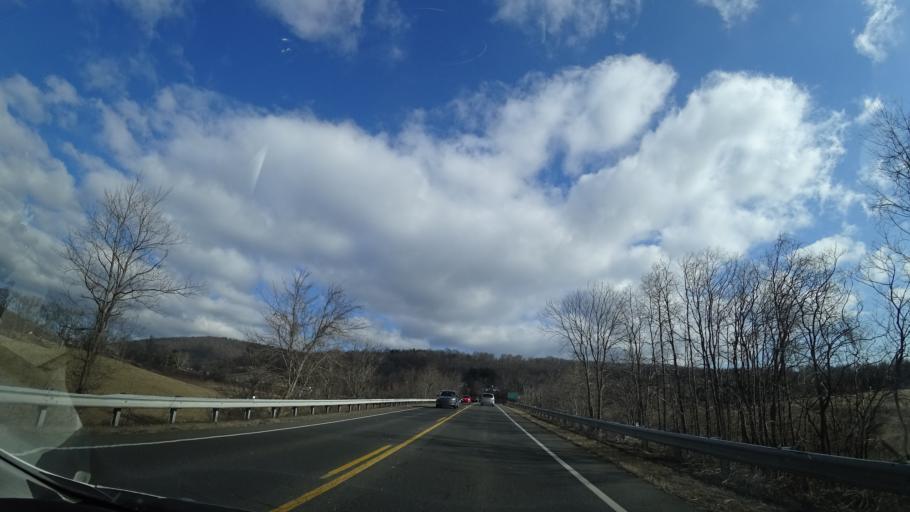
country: US
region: Virginia
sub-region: Warren County
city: Shenandoah Farms
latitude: 39.0012
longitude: -77.9476
